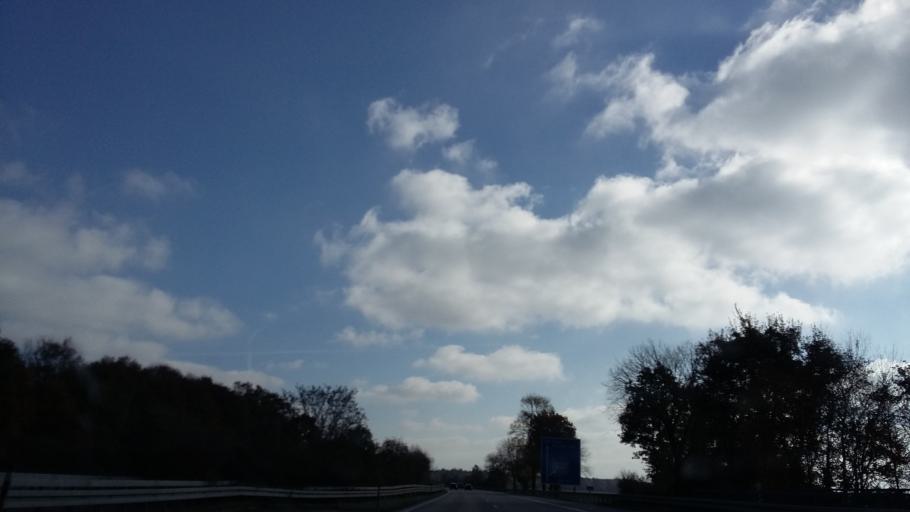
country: DE
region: Bavaria
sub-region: Upper Bavaria
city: Taufkirchen
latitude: 48.0307
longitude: 11.6172
